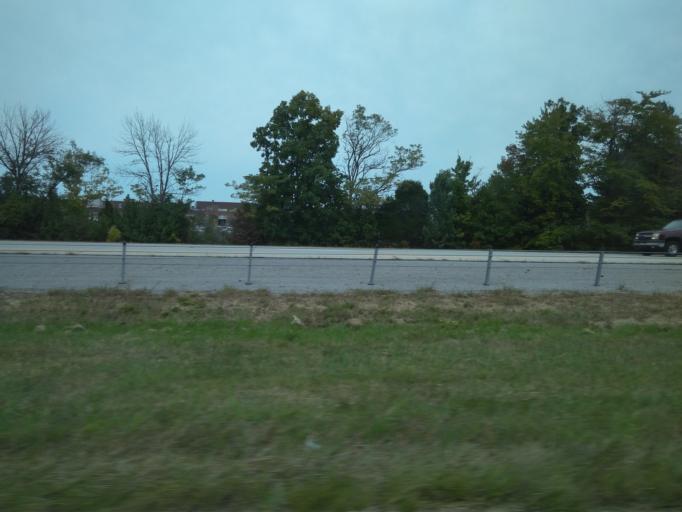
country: US
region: Kentucky
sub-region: Jefferson County
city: Worthington Hills
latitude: 38.2905
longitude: -85.5375
